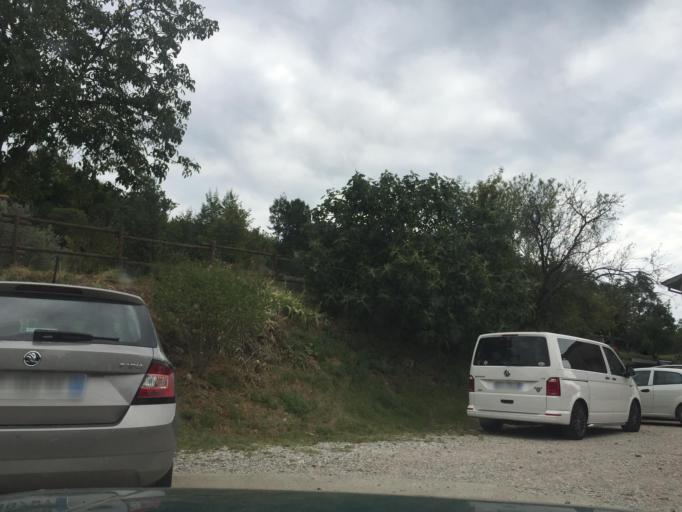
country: IT
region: Friuli Venezia Giulia
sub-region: Provincia di Trieste
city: Duino
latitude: 45.7965
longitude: 13.6020
